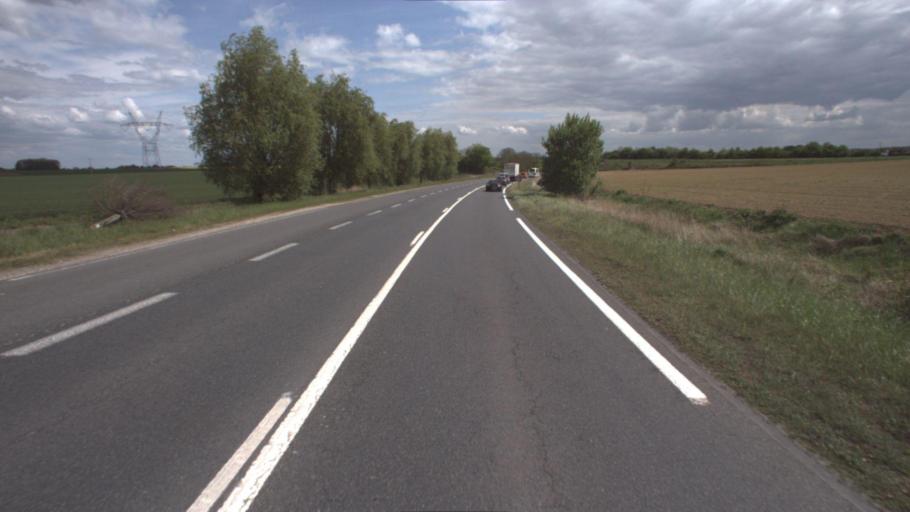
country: FR
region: Ile-de-France
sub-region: Departement de Seine-et-Marne
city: Cregy-les-Meaux
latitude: 48.9915
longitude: 2.8652
